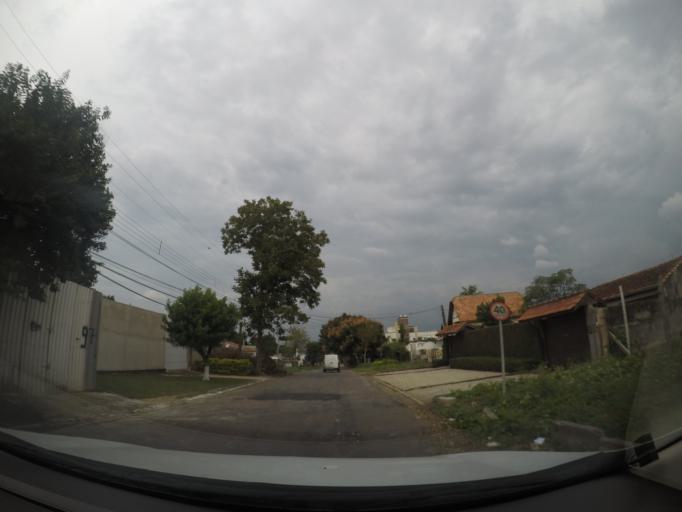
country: BR
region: Parana
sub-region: Sao Jose Dos Pinhais
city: Sao Jose dos Pinhais
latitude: -25.5217
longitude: -49.2371
